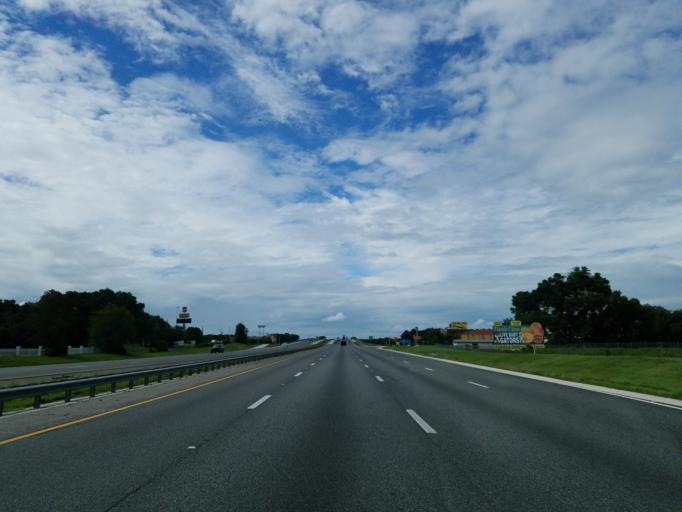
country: US
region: Florida
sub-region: Marion County
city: Belleview
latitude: 29.0205
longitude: -82.1559
